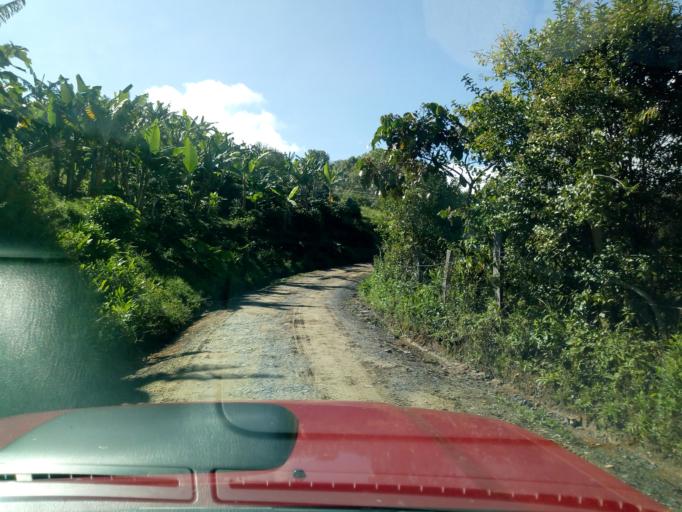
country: CO
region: Boyaca
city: Moniquira
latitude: 5.8912
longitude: -73.5245
